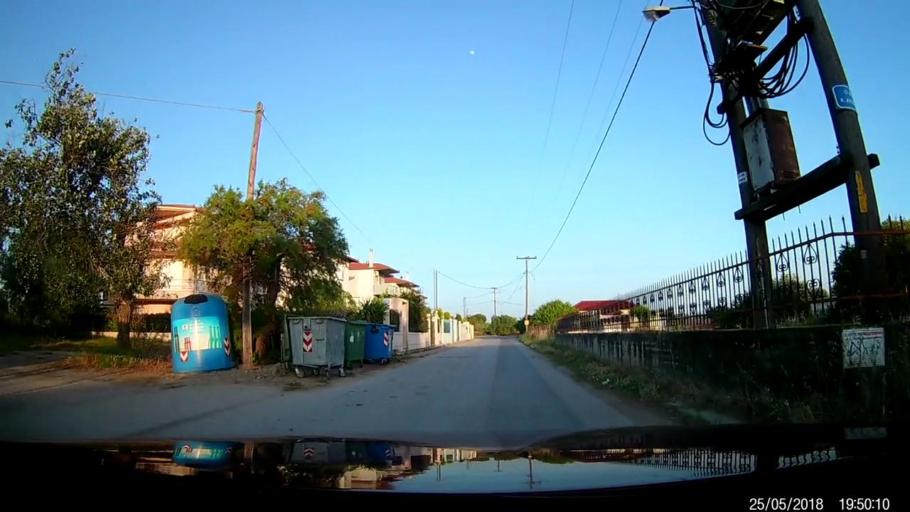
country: GR
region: Central Greece
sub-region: Nomos Evvoias
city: Ayios Nikolaos
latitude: 38.4082
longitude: 23.6401
